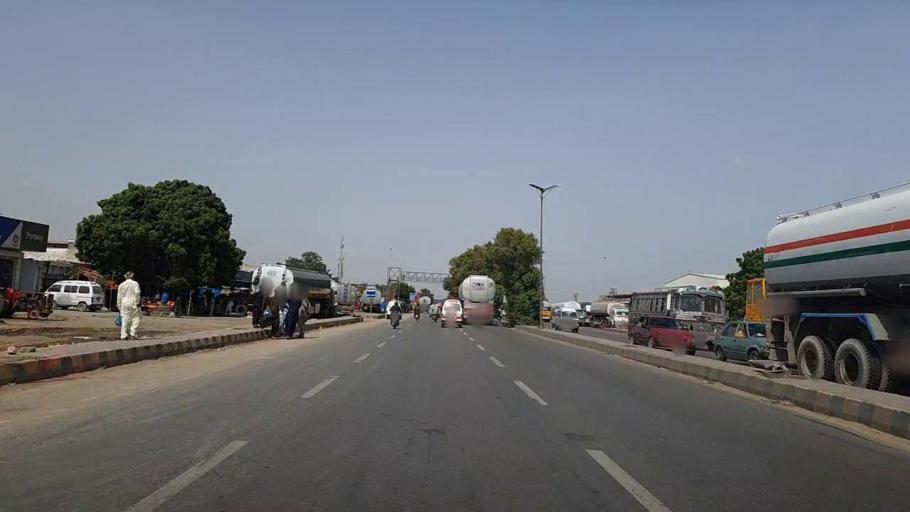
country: PK
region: Sindh
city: Malir Cantonment
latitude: 24.8644
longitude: 67.2926
